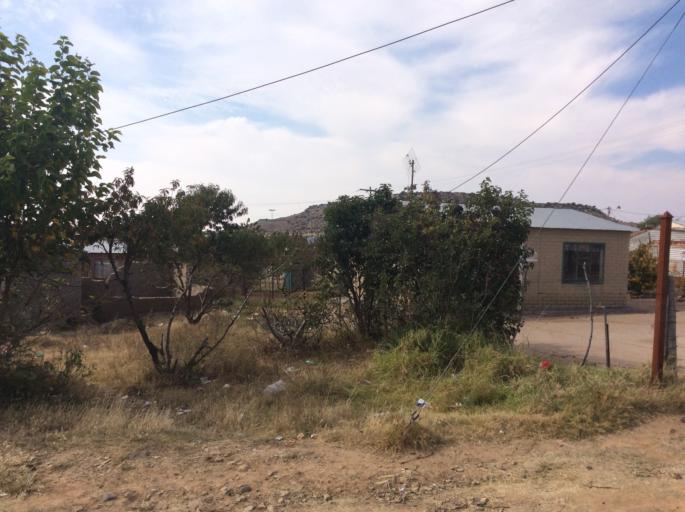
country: ZA
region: Orange Free State
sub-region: Xhariep District Municipality
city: Dewetsdorp
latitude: -29.5927
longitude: 26.6799
